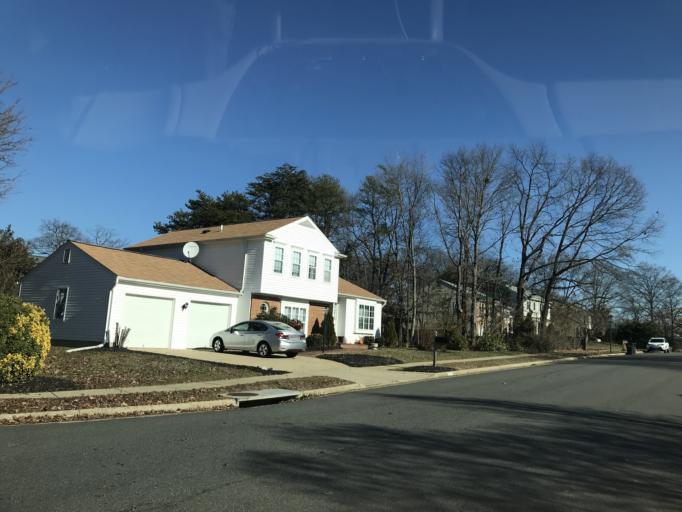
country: US
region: Virginia
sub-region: Fairfax County
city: Franconia
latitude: 38.7834
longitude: -77.1548
